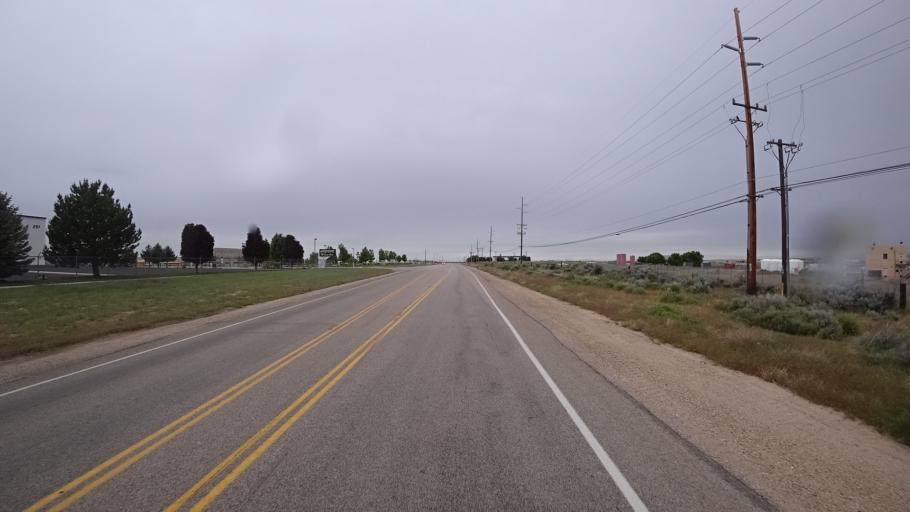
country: US
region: Idaho
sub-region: Ada County
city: Boise
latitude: 43.5461
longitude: -116.1843
